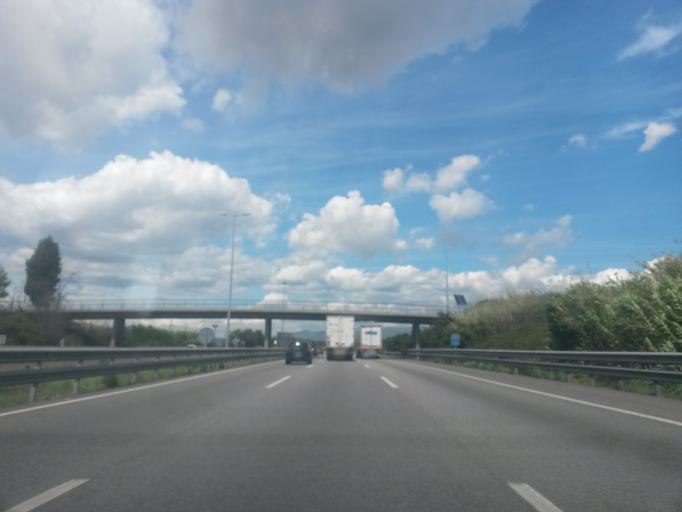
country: ES
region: Catalonia
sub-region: Provincia de Barcelona
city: Granollers
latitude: 41.5732
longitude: 2.2846
